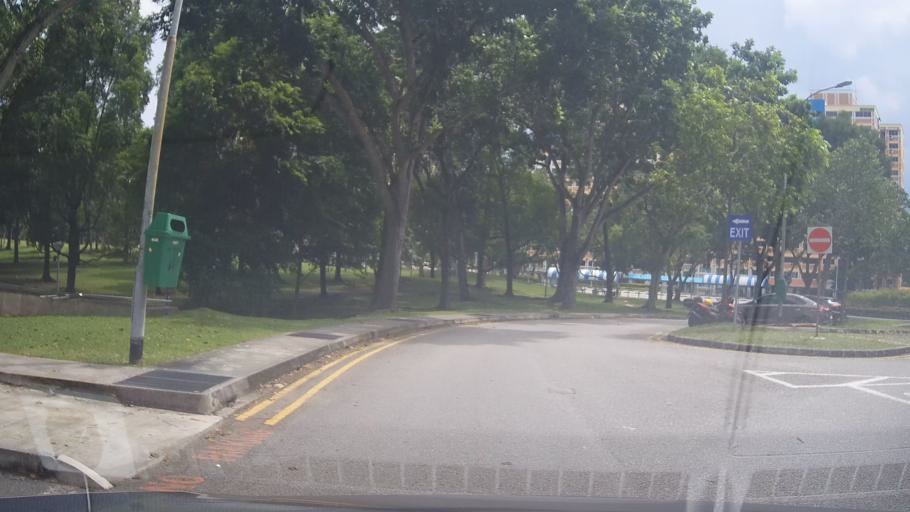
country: MY
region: Johor
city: Kampung Pasir Gudang Baru
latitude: 1.3708
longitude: 103.9513
